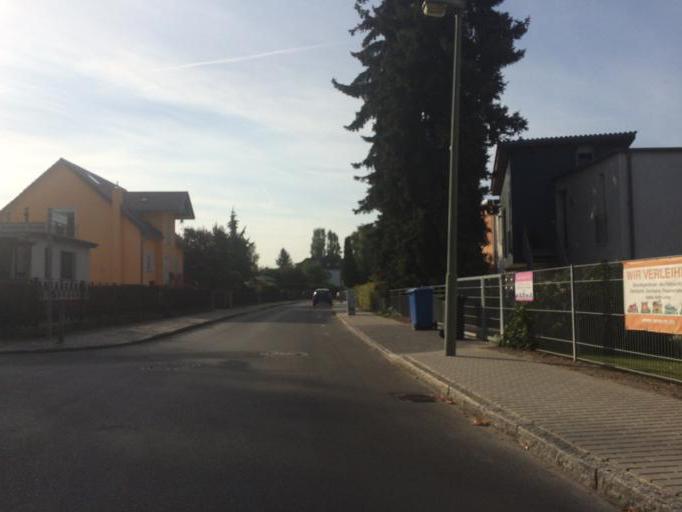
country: DE
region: Berlin
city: Alt-Hohenschoenhausen
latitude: 52.5560
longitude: 13.4967
